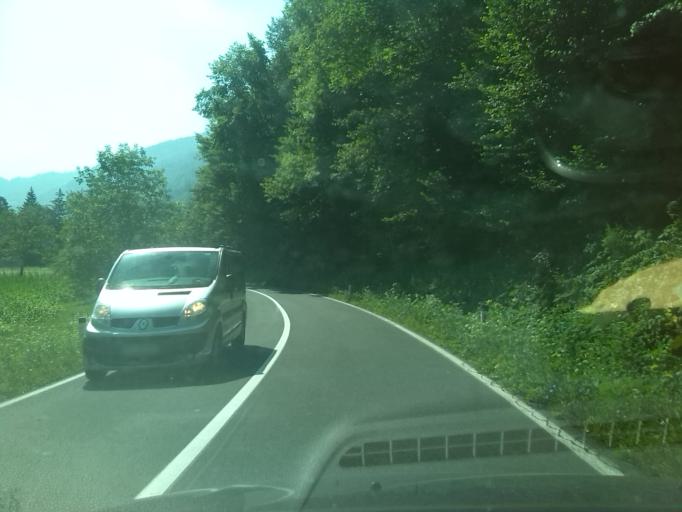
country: SI
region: Kobarid
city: Kobarid
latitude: 46.2191
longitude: 13.6081
